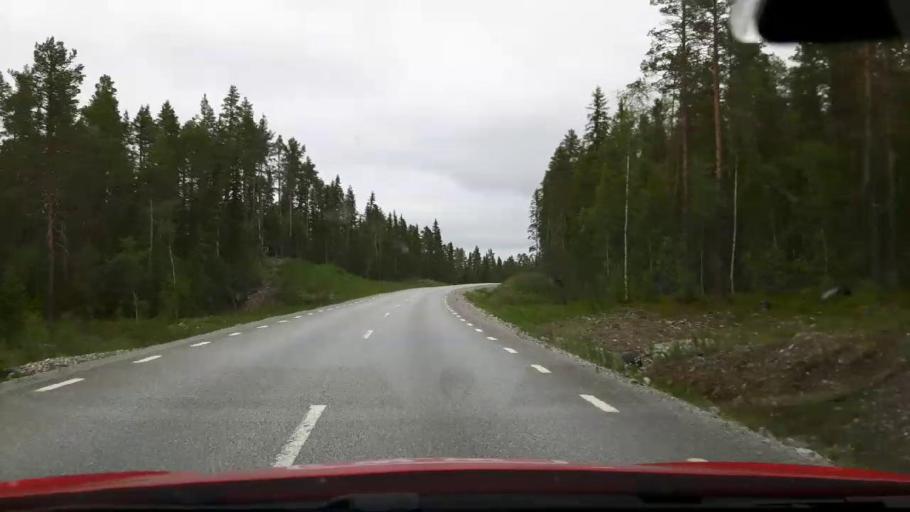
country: SE
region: Jaemtland
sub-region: OEstersunds Kommun
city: Lit
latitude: 63.7107
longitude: 14.6964
